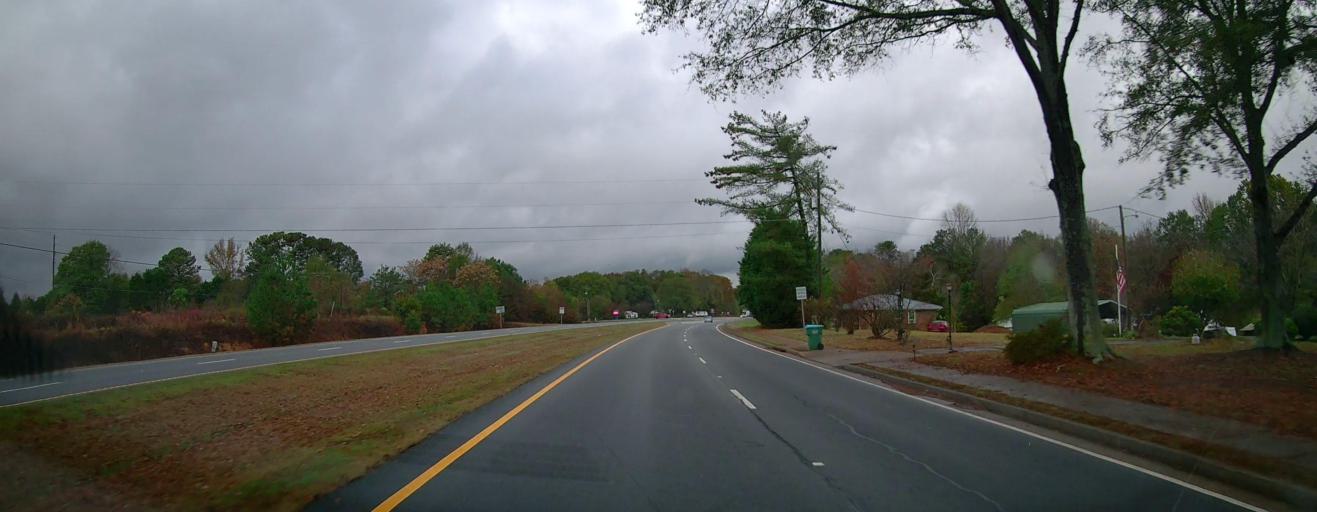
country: US
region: Georgia
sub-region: Jackson County
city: Nicholson
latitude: 34.0991
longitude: -83.4323
